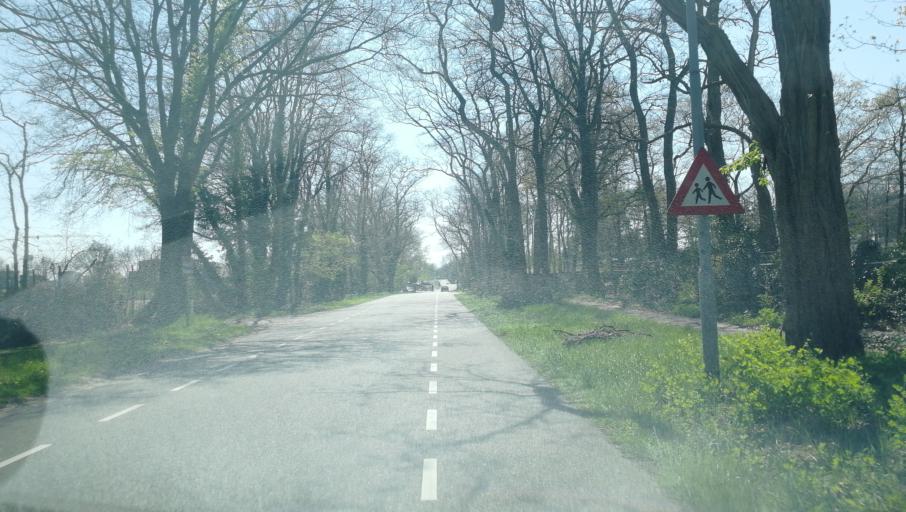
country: NL
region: Limburg
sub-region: Gemeente Venlo
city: Venlo
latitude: 51.3676
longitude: 6.2002
